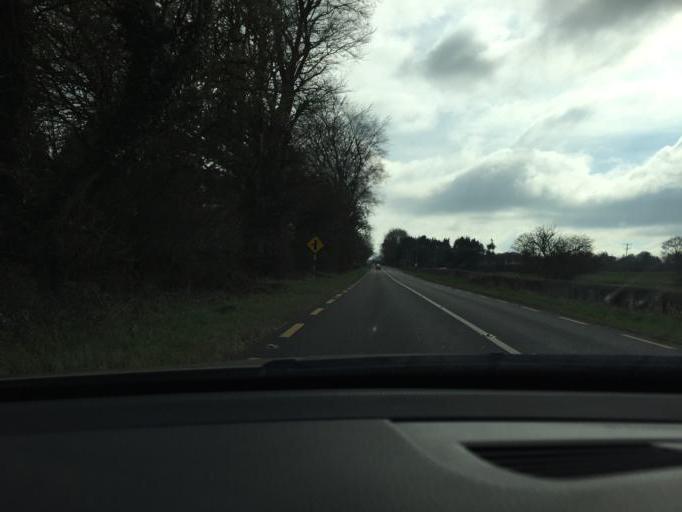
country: IE
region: Leinster
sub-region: Wicklow
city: Blessington
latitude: 53.1528
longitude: -6.5542
